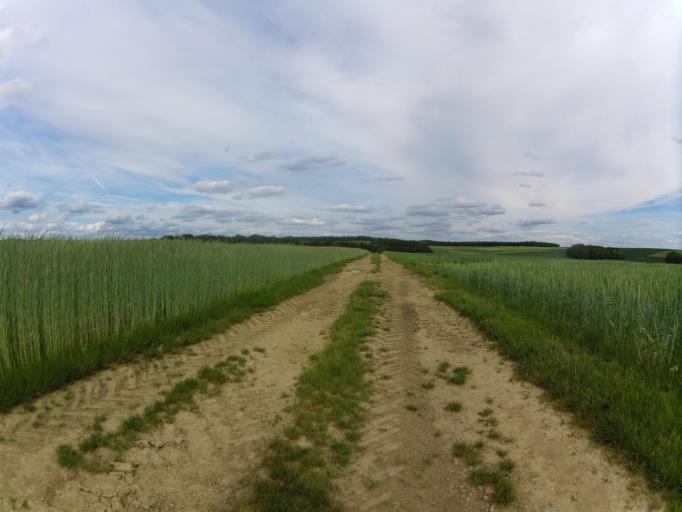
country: DE
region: Bavaria
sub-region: Regierungsbezirk Unterfranken
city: Frickenhausen
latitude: 49.7000
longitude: 10.0780
